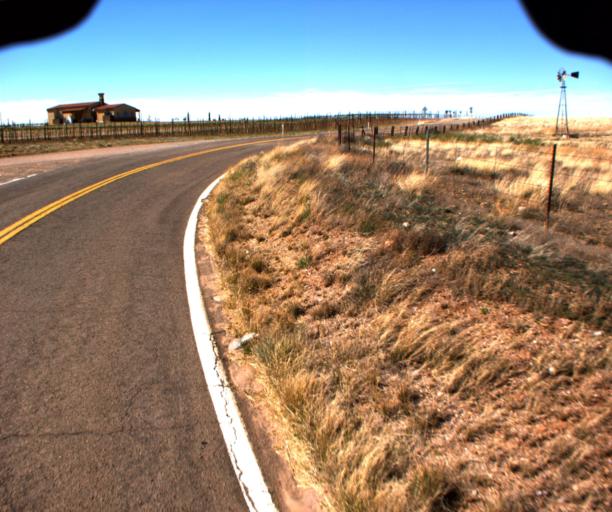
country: US
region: Arizona
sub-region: Cochise County
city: Huachuca City
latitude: 31.6083
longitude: -110.5868
